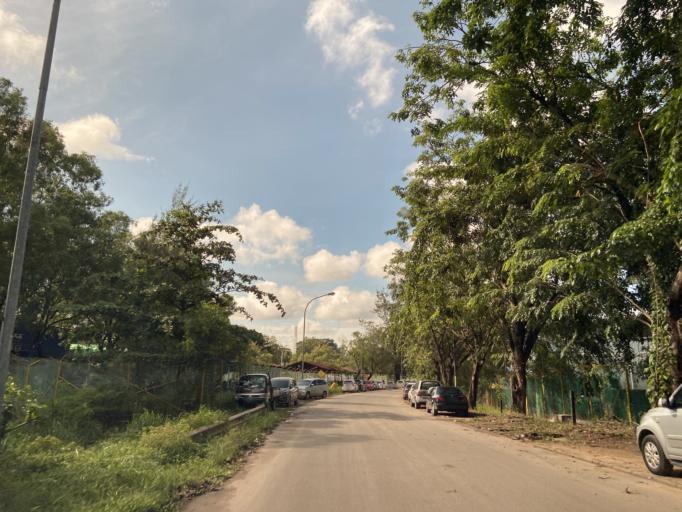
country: SG
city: Singapore
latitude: 1.1752
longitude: 104.0071
